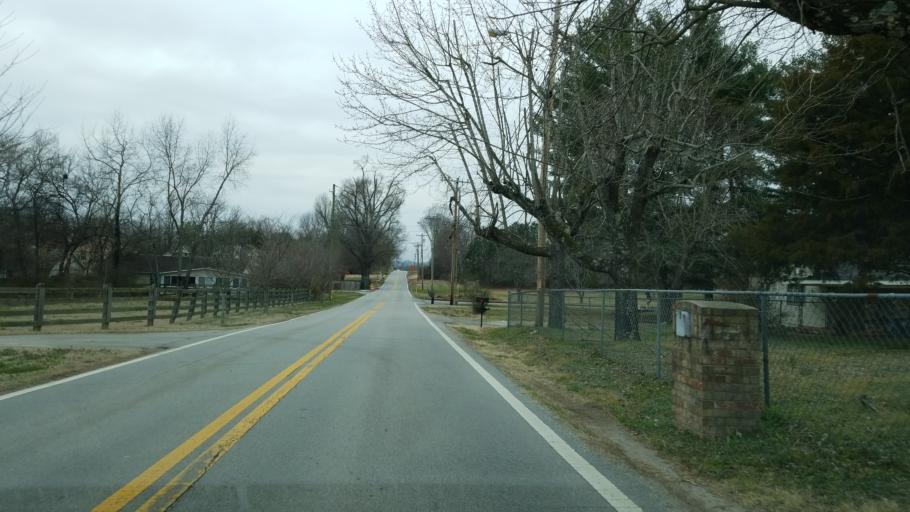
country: US
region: Tennessee
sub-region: Hamilton County
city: East Brainerd
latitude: 35.0546
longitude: -85.1562
